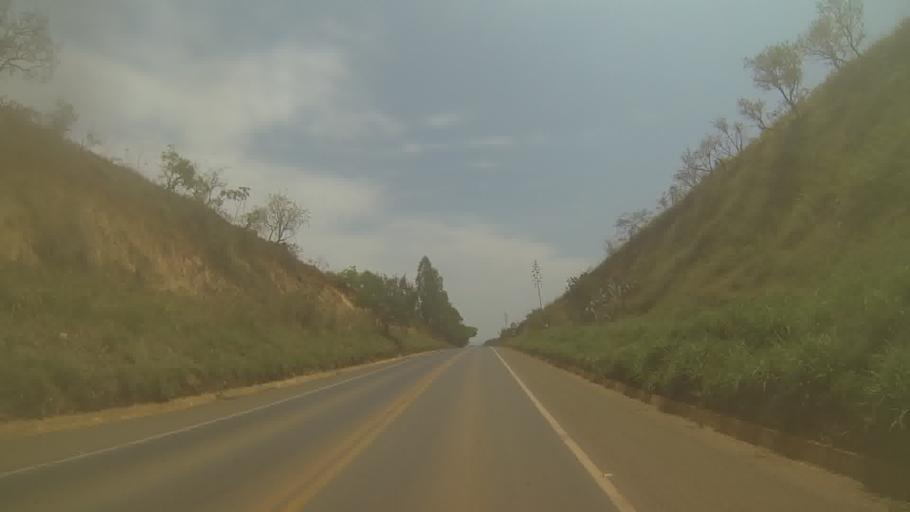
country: BR
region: Minas Gerais
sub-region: Bambui
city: Bambui
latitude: -20.0154
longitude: -45.9419
